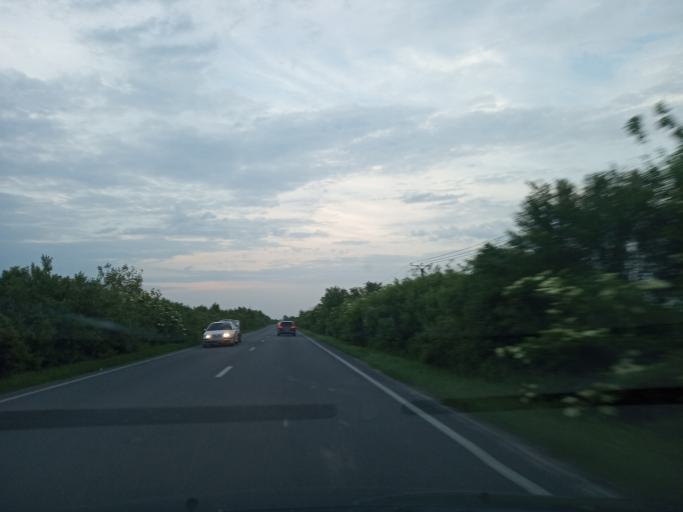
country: RO
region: Timis
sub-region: Oras Deta
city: Deta
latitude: 45.4248
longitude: 21.2300
